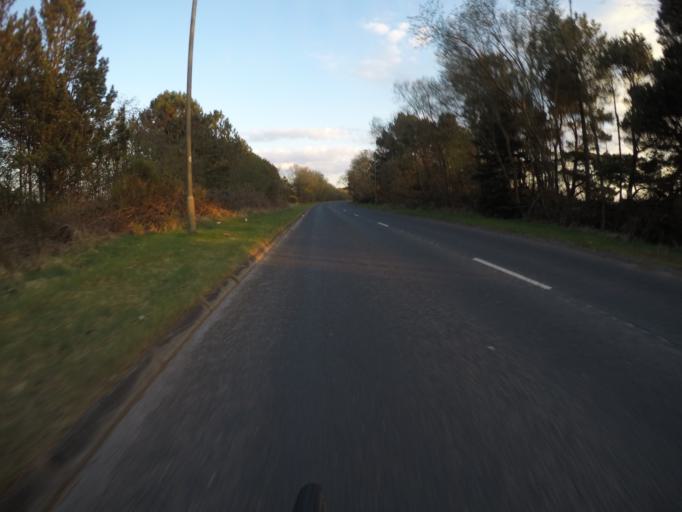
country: GB
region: Scotland
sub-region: North Ayrshire
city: Irvine
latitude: 55.5941
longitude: -4.6682
